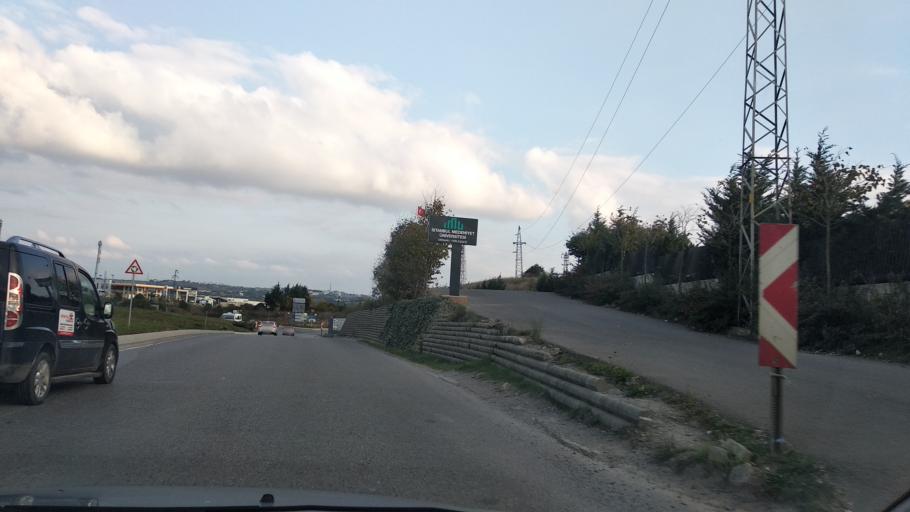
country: TR
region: Istanbul
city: Sultanbeyli
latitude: 40.9270
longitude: 29.3469
